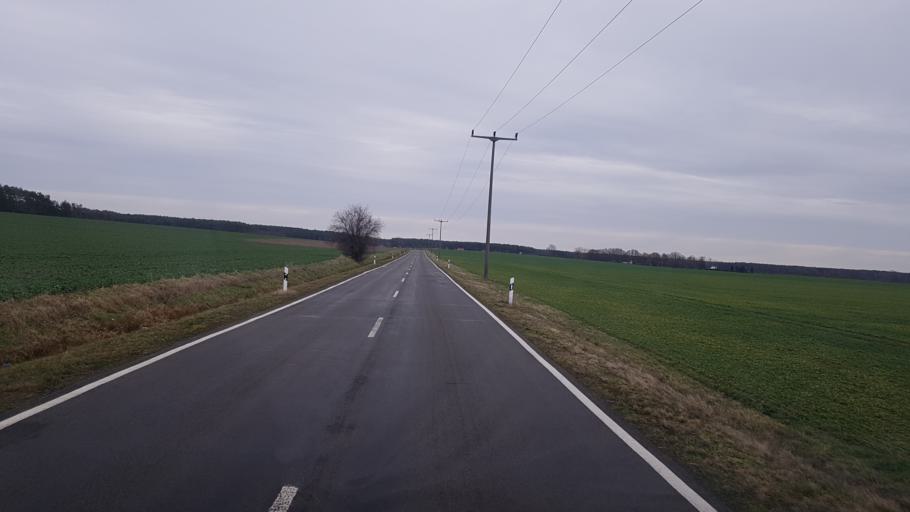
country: DE
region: Brandenburg
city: Sonnewalde
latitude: 51.7076
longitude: 13.7024
